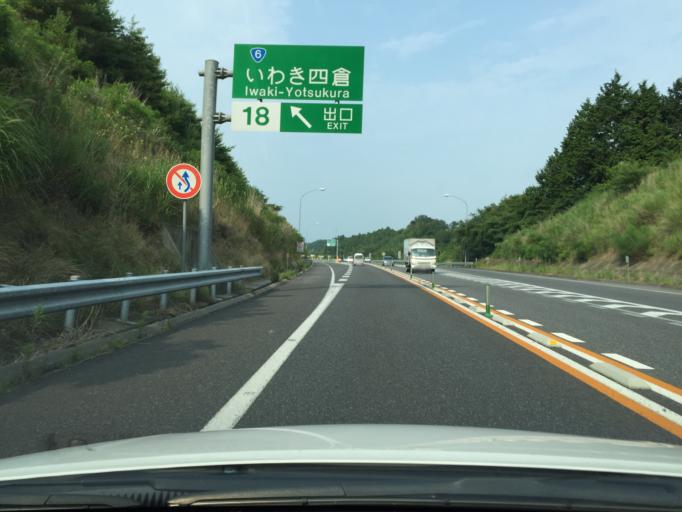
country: JP
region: Fukushima
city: Iwaki
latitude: 37.1254
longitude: 140.9426
